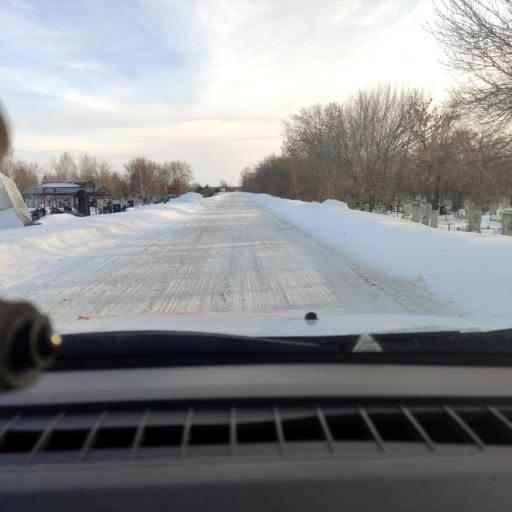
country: RU
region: Samara
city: Chapayevsk
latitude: 52.9910
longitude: 49.7437
